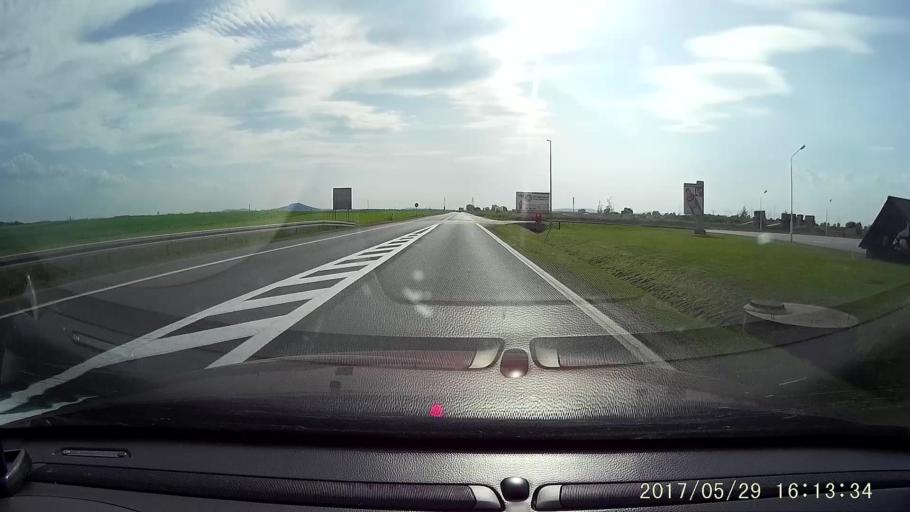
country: PL
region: Lower Silesian Voivodeship
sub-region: Powiat zgorzelecki
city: Lagow
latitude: 51.1848
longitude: 15.0500
